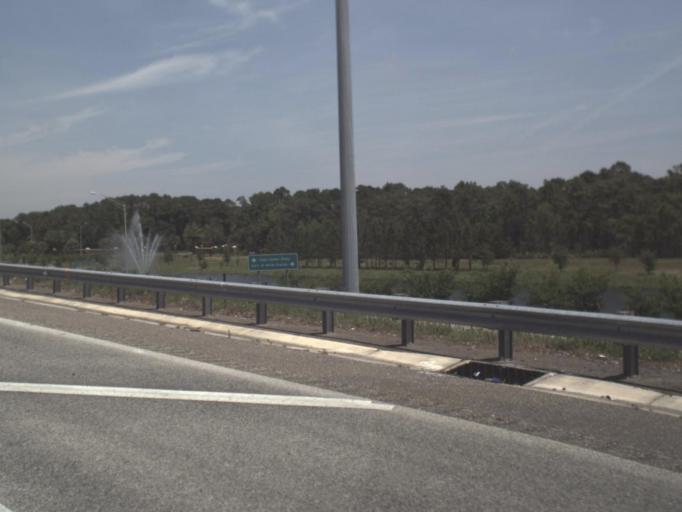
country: US
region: Florida
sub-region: Duval County
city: Jacksonville Beach
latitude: 30.2659
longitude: -81.5197
